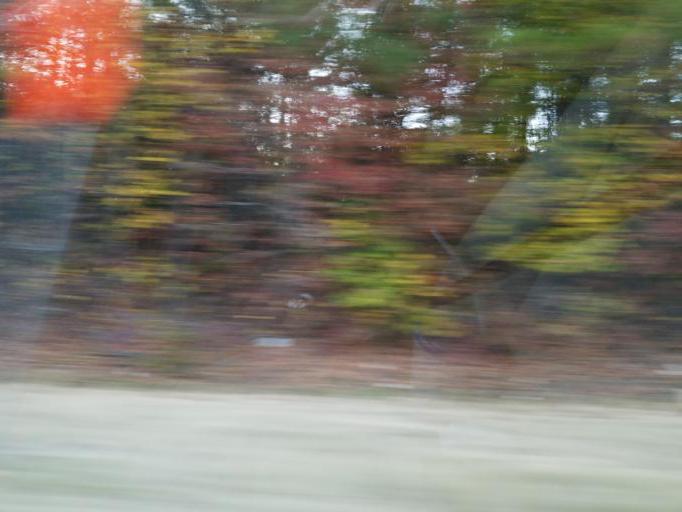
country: US
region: Georgia
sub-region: Dawson County
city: Dawsonville
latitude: 34.3709
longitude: -84.0305
